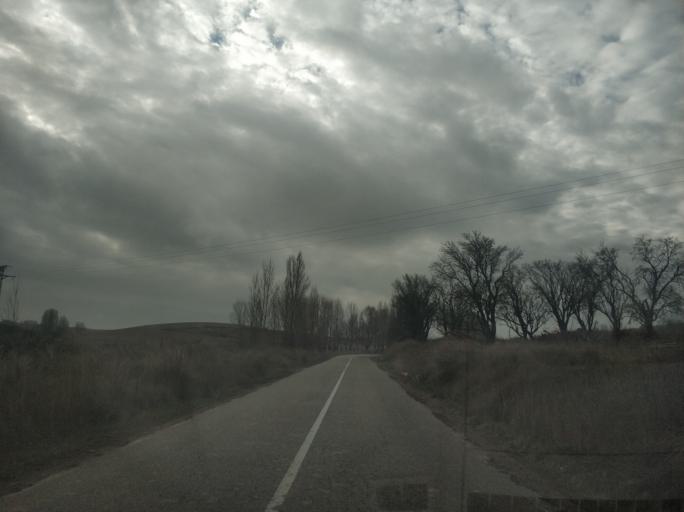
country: ES
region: Castille and Leon
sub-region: Provincia de Burgos
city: Penaranda de Duero
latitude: 41.6787
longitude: -3.4798
